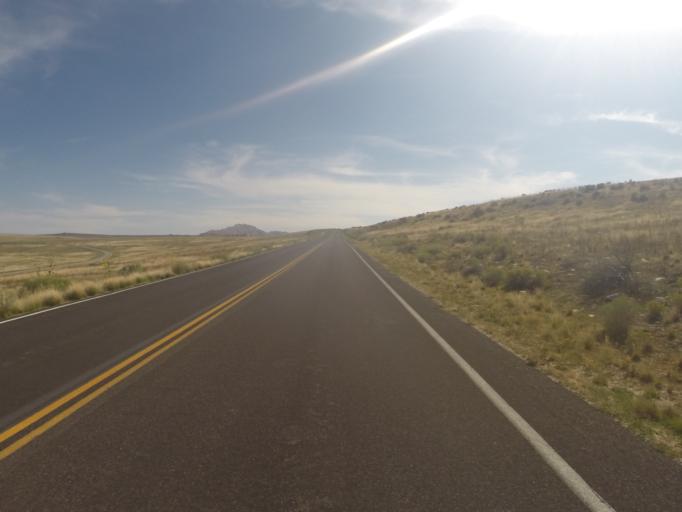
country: US
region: Utah
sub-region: Weber County
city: Hooper
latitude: 41.0501
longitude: -112.2365
